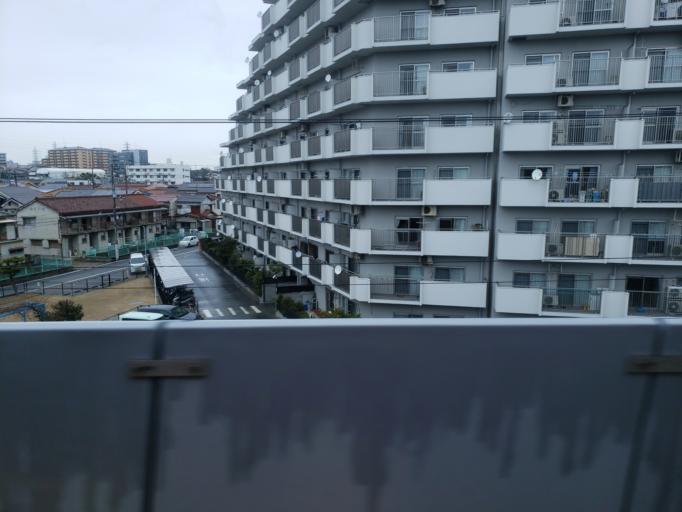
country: JP
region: Hyogo
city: Akashi
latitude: 34.6494
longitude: 134.9757
